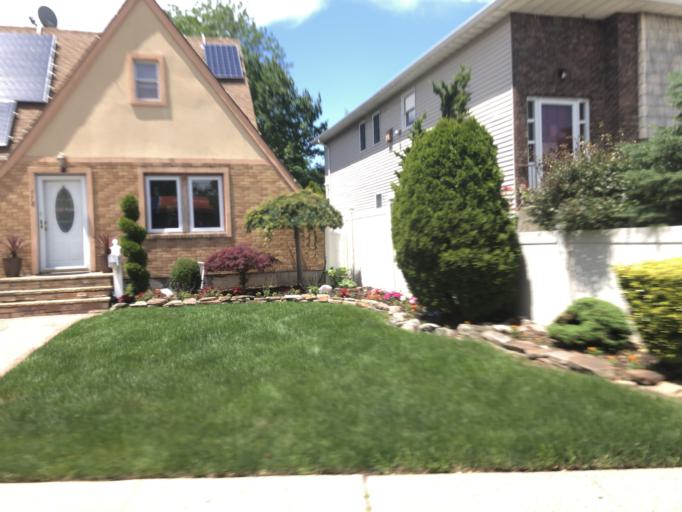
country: US
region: New York
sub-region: Nassau County
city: Uniondale
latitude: 40.6951
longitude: -73.5951
